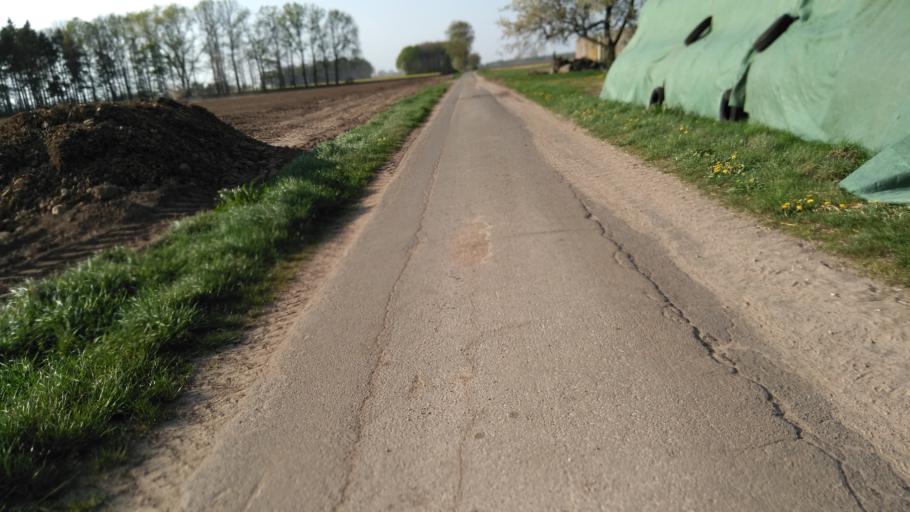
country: DE
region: Lower Saxony
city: Apensen
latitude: 53.4283
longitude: 9.6504
